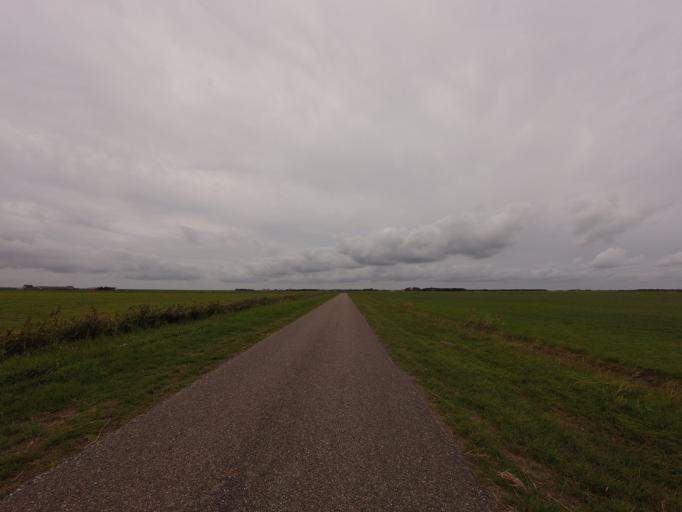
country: NL
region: Friesland
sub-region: Gemeente Ameland
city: Hollum
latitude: 53.4325
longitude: 5.6850
